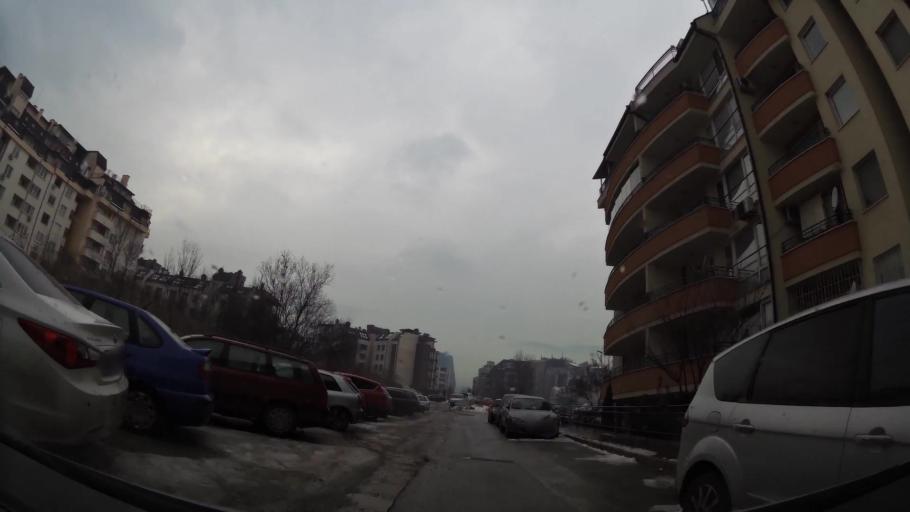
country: BG
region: Sofia-Capital
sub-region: Stolichna Obshtina
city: Sofia
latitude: 42.6619
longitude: 23.2898
